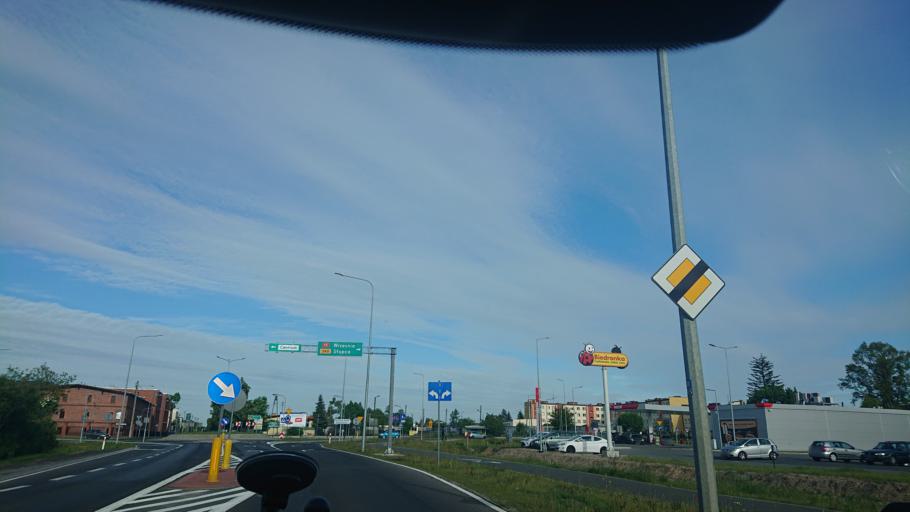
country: PL
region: Greater Poland Voivodeship
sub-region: Powiat gnieznienski
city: Gniezno
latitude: 52.5140
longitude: 17.5934
